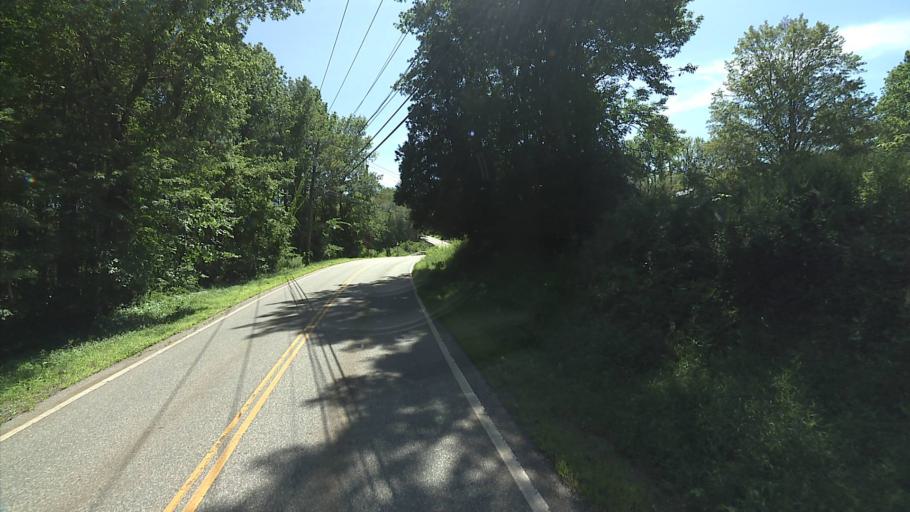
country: US
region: Connecticut
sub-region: Windham County
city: Windham
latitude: 41.7650
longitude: -72.0585
